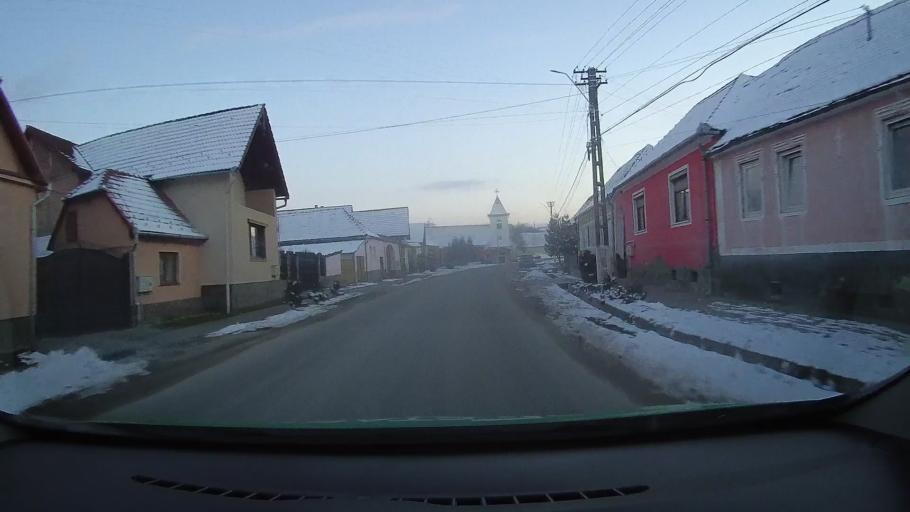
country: RO
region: Sibiu
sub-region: Comuna Alma
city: Alma
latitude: 46.1987
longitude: 24.4450
